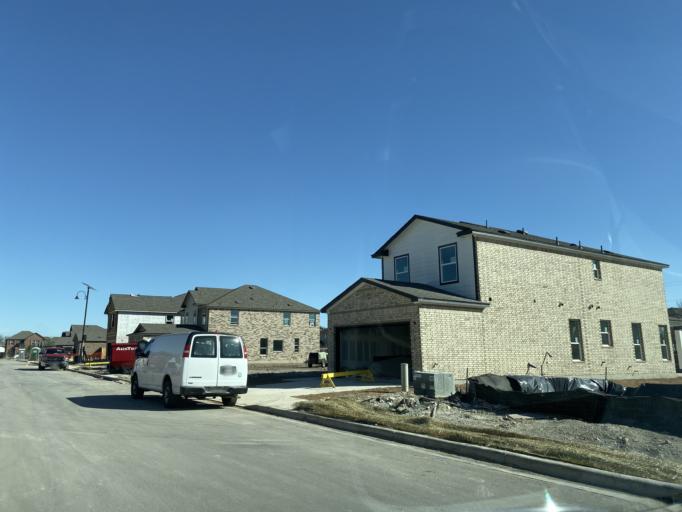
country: US
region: Texas
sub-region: Travis County
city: Windemere
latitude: 30.4743
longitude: -97.6559
